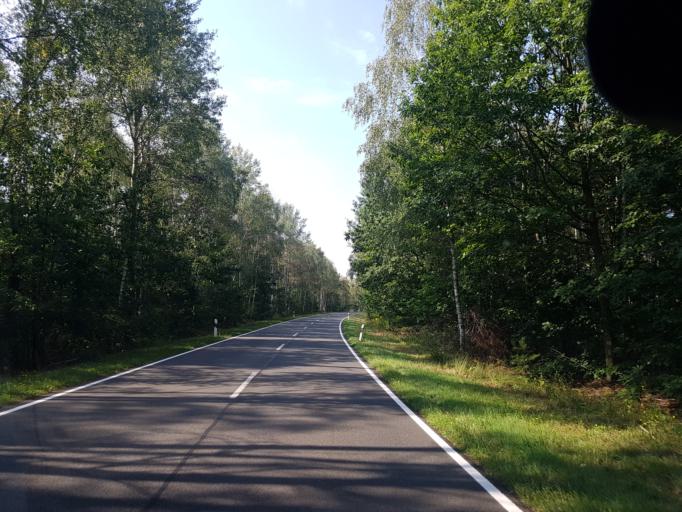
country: DE
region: Brandenburg
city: Lauchhammer
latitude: 51.5233
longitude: 13.7134
